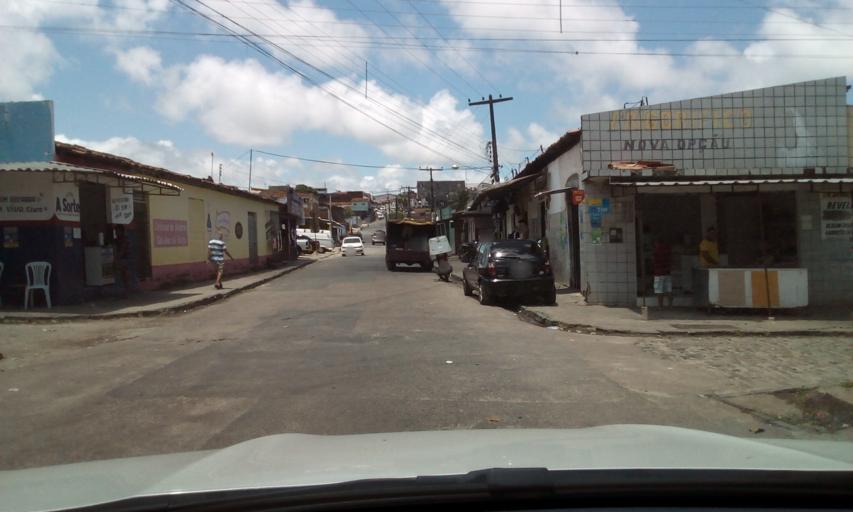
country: BR
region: Paraiba
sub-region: Joao Pessoa
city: Joao Pessoa
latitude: -7.0994
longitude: -34.8625
